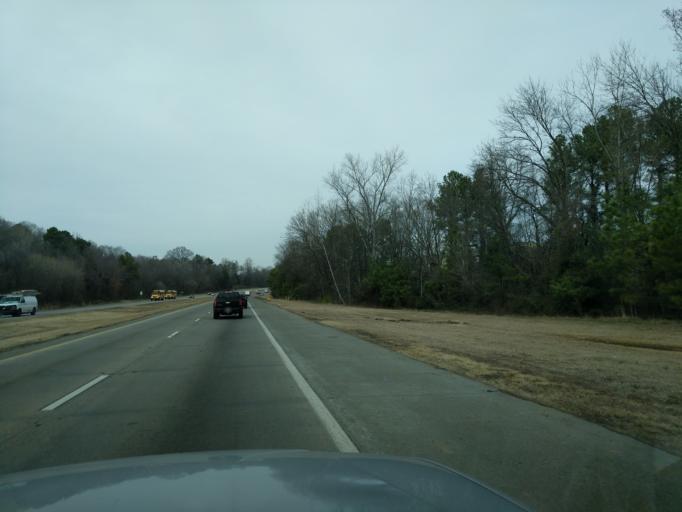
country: US
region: North Carolina
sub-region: Mecklenburg County
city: Charlotte
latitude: 35.2071
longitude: -80.9224
